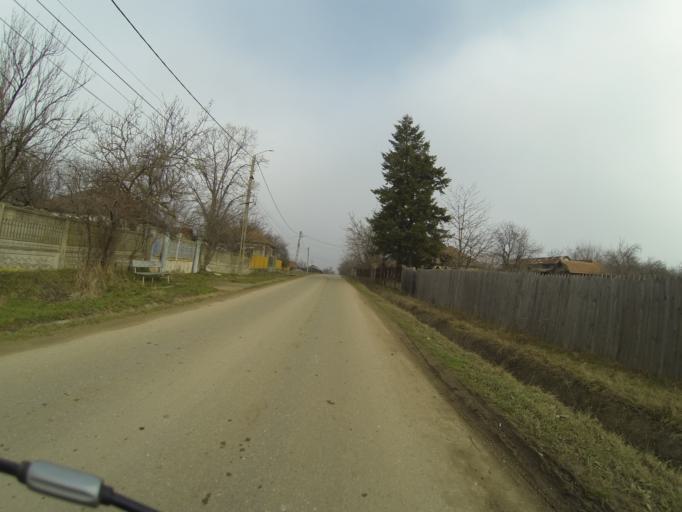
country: RO
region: Mehedinti
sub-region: Comuna Balacita
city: Gvardinita
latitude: 44.3917
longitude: 23.1428
